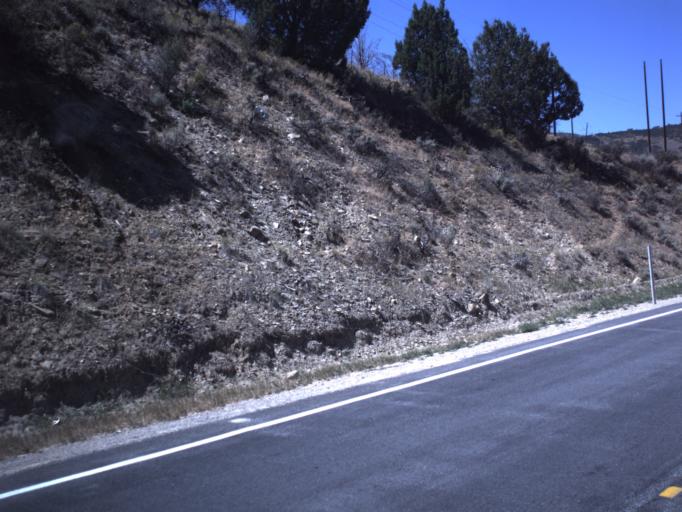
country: US
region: Utah
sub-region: Summit County
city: Oakley
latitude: 40.7555
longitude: -111.3847
